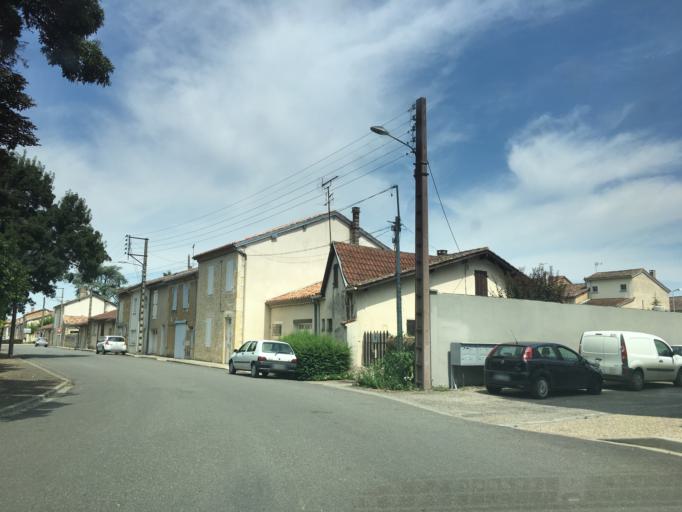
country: FR
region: Midi-Pyrenees
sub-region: Departement du Gers
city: Fleurance
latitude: 43.8444
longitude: 0.6606
